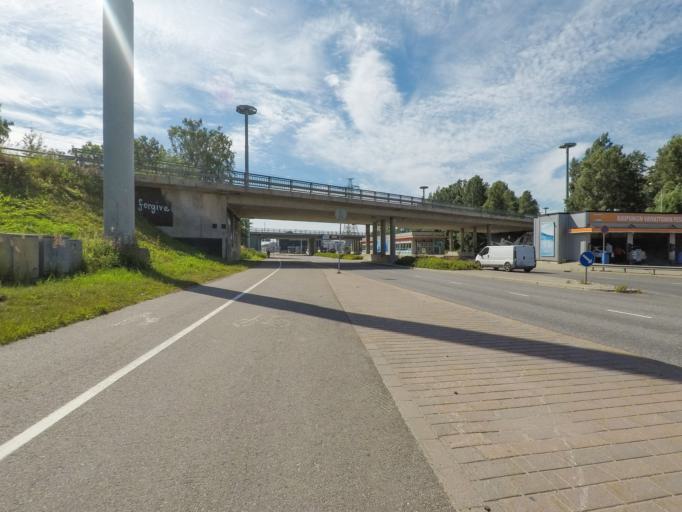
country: FI
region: Uusimaa
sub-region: Helsinki
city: Vantaa
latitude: 60.2084
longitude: 25.0558
